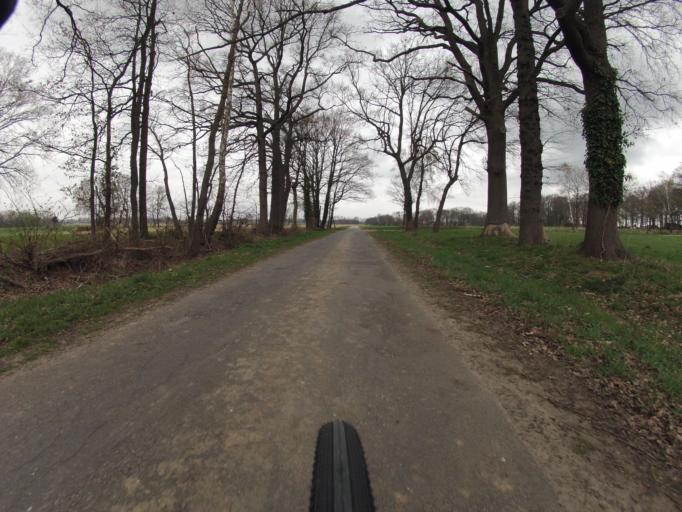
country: DE
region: North Rhine-Westphalia
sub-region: Regierungsbezirk Munster
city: Mettingen
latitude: 52.3339
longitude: 7.8186
